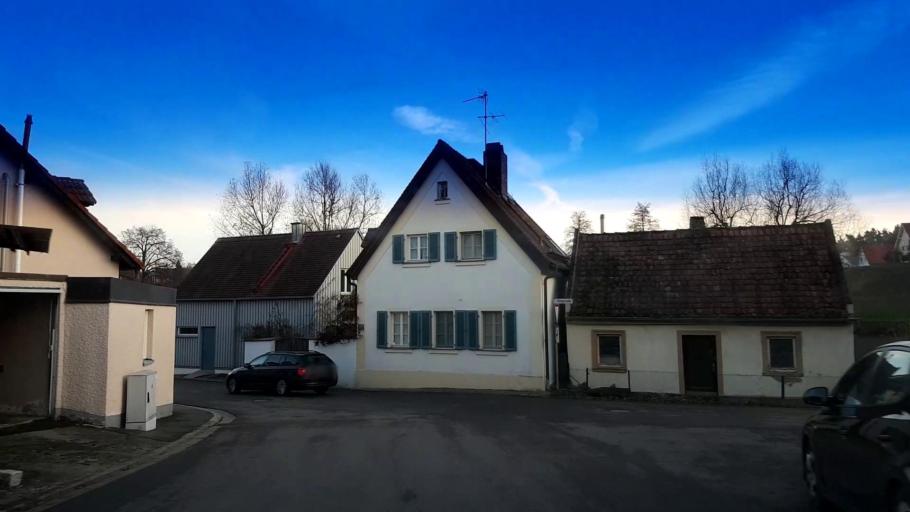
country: DE
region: Bavaria
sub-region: Upper Franconia
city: Stegaurach
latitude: 49.8600
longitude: 10.8230
